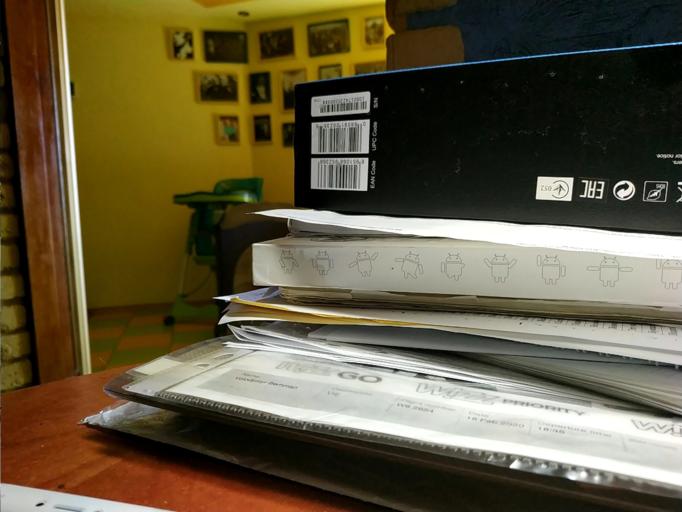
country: RU
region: Vologda
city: Vytegra
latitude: 60.8533
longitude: 36.7377
